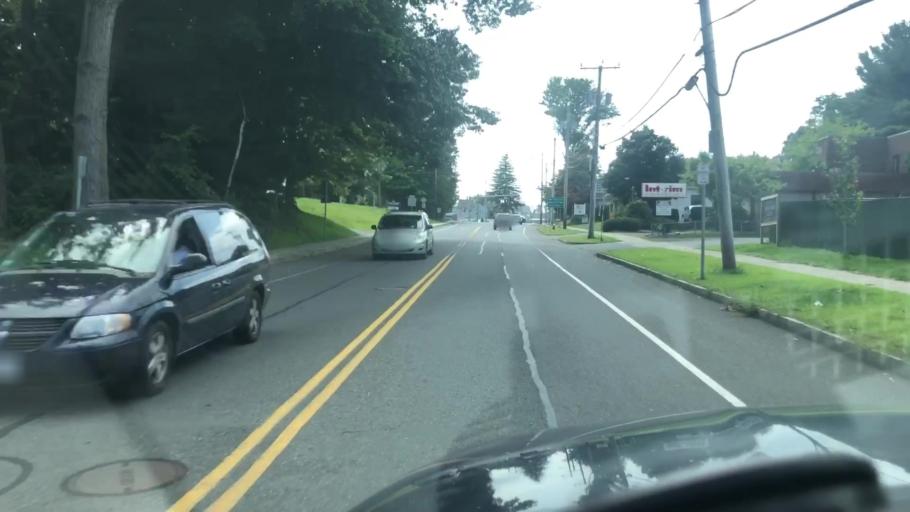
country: US
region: Massachusetts
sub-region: Hampden County
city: West Springfield
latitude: 42.1048
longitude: -72.6300
